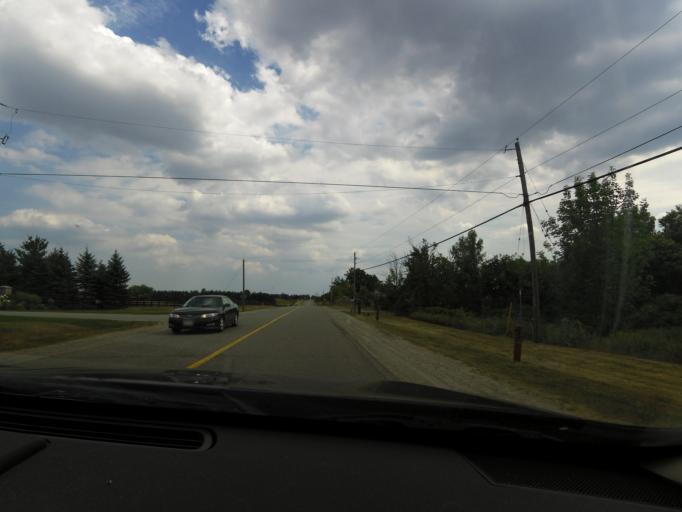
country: CA
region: Ontario
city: Brampton
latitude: 43.7471
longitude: -79.9147
